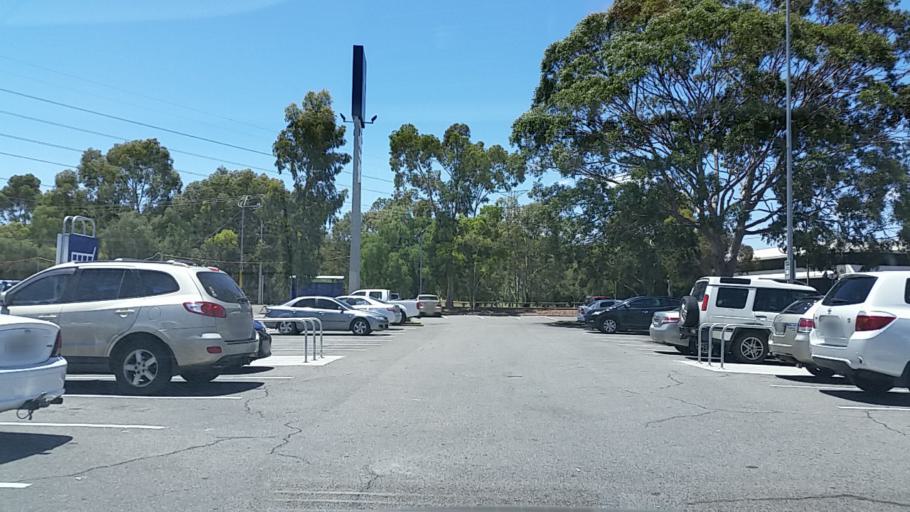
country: AU
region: South Australia
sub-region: Salisbury
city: Salisbury
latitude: -34.7604
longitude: 138.6478
